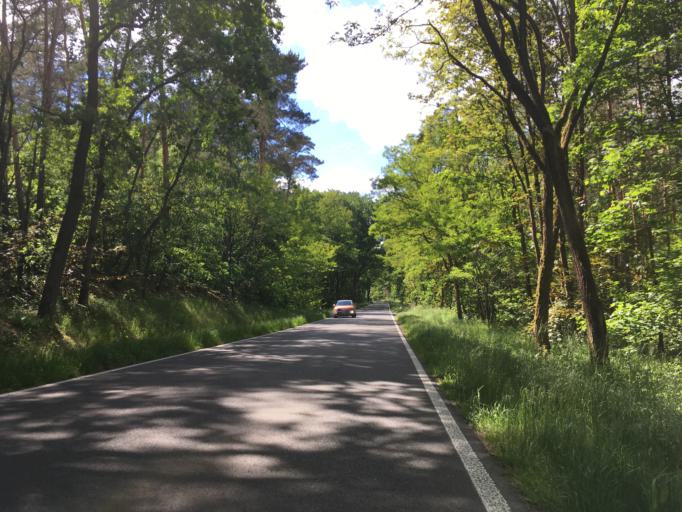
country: DE
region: Brandenburg
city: Protzel
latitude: 52.6011
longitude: 13.9946
